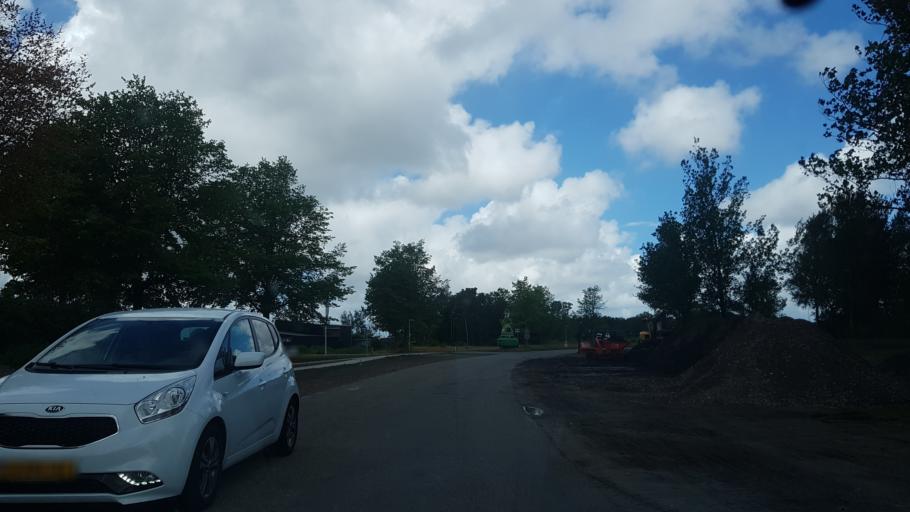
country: NL
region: Friesland
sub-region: Gemeente Dongeradeel
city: Anjum
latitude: 53.4036
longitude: 6.2140
